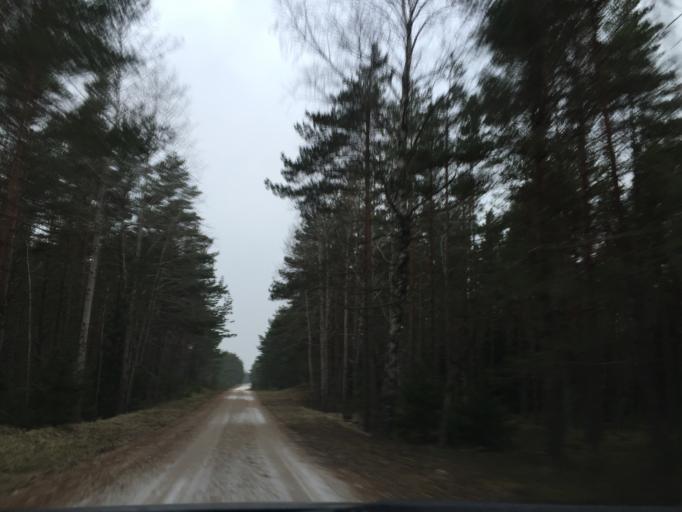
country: EE
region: Saare
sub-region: Kuressaare linn
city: Kuressaare
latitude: 58.4075
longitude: 22.1975
